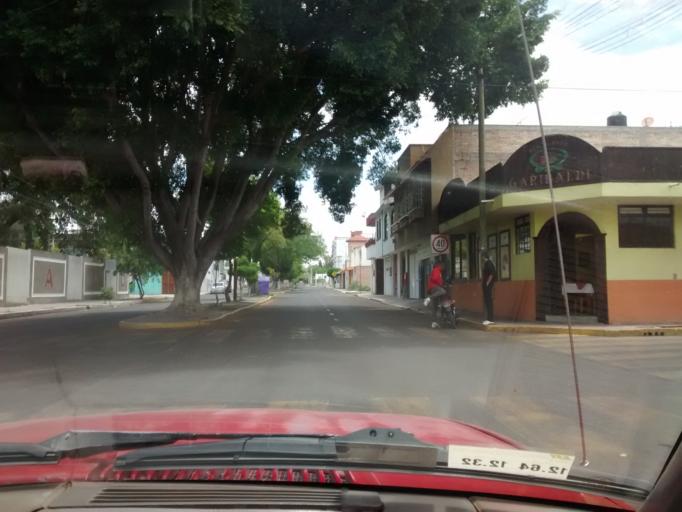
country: MX
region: Puebla
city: Tehuacan
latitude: 18.4614
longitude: -97.4078
